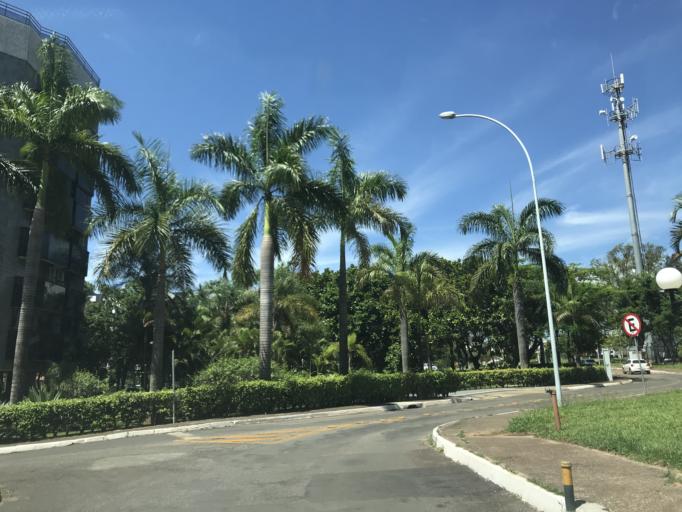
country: BR
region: Federal District
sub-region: Brasilia
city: Brasilia
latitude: -15.8024
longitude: -47.9255
